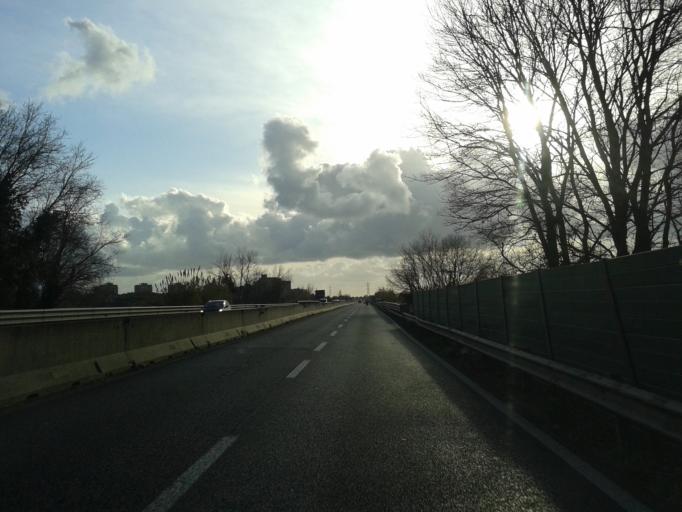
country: IT
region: Tuscany
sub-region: Provincia di Livorno
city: Livorno
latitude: 43.5446
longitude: 10.3402
